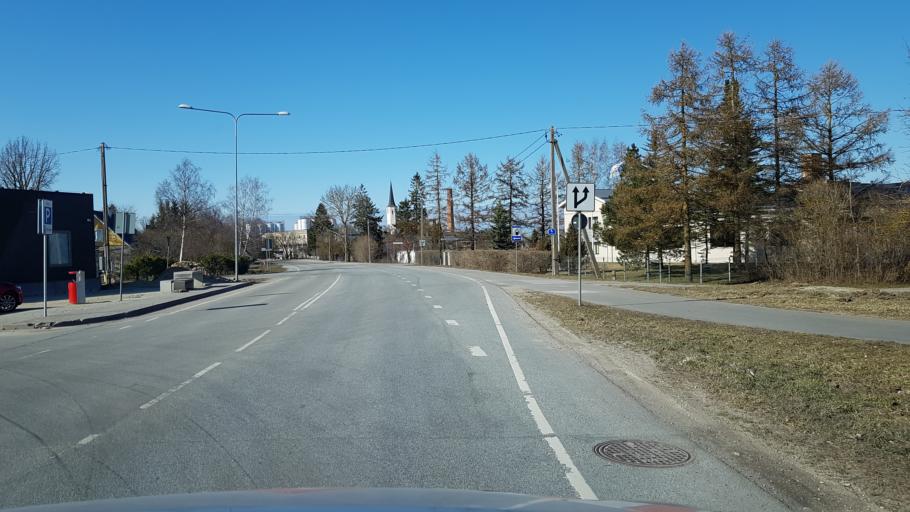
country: EE
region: Laeaene-Virumaa
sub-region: Haljala vald
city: Haljala
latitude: 59.4265
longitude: 26.2699
